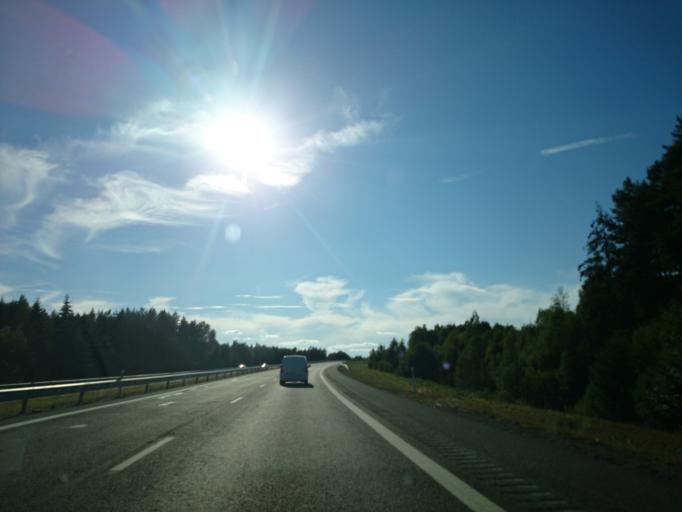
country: SE
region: Soedermanland
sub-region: Nykopings Kommun
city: Svalsta
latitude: 58.7506
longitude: 16.8839
